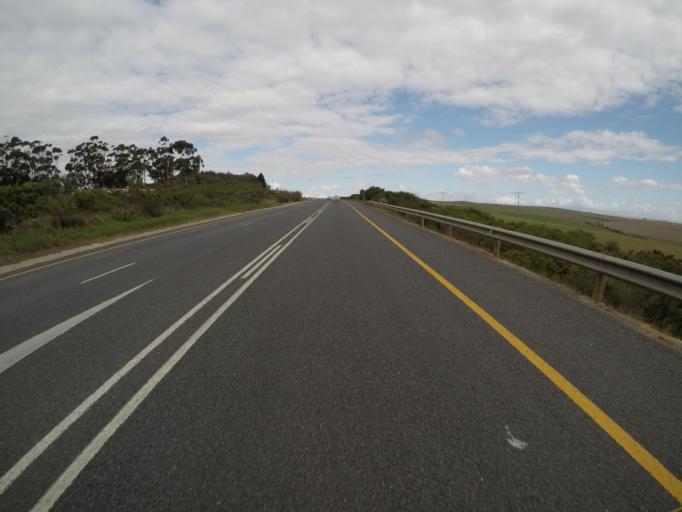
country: ZA
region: Western Cape
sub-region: Overberg District Municipality
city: Swellendam
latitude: -34.0712
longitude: 20.6213
